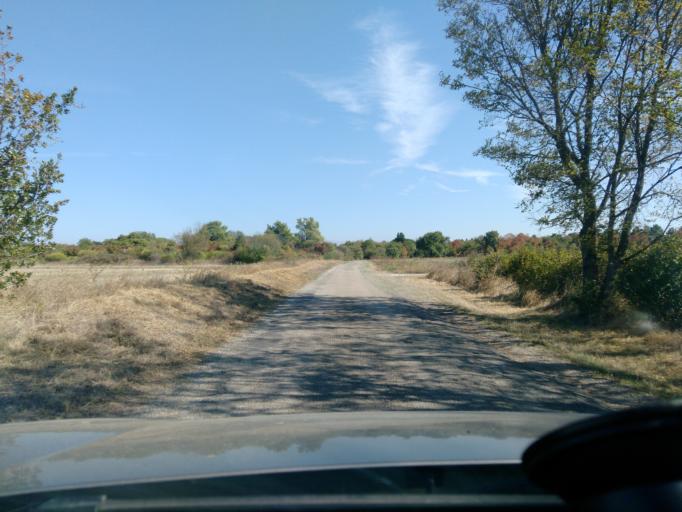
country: FR
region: Rhone-Alpes
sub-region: Departement de la Drome
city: Montboucher-sur-Jabron
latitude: 44.5541
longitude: 4.7812
